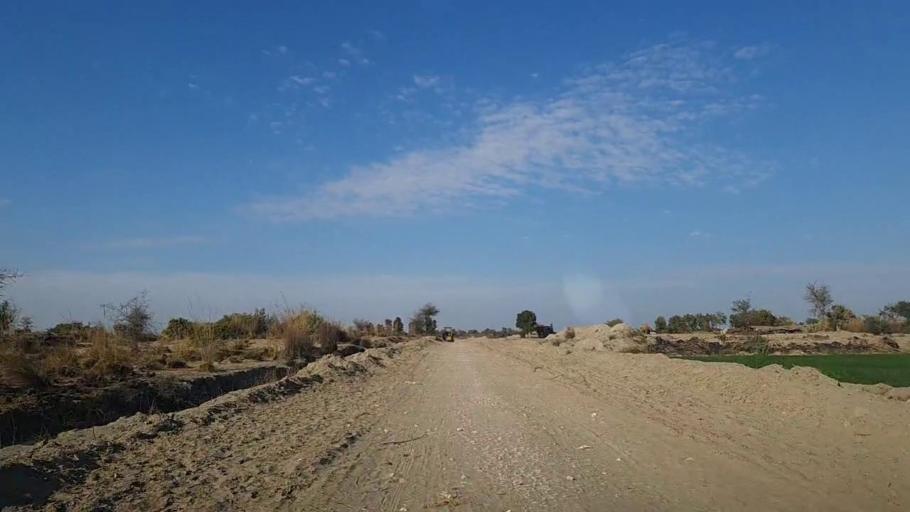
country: PK
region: Sindh
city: Khadro
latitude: 26.3052
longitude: 68.8383
